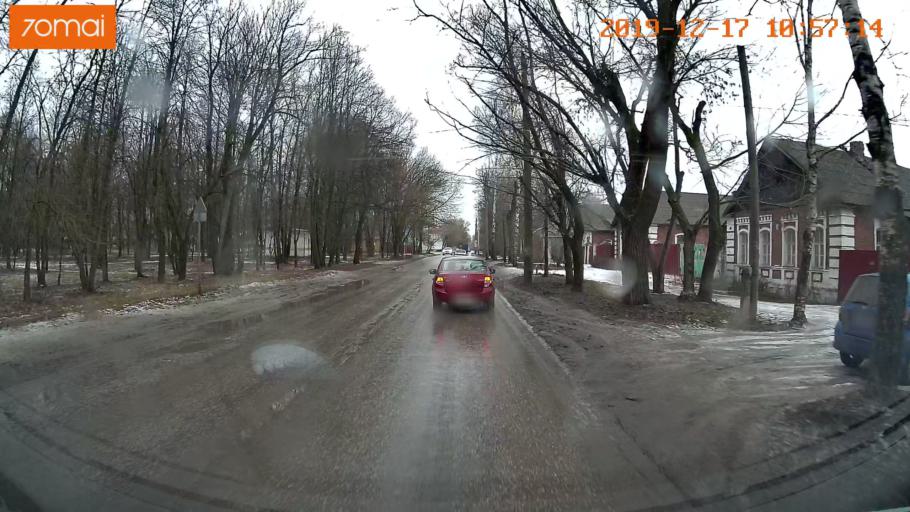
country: RU
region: Vladimir
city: Gus'-Khrustal'nyy
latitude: 55.6205
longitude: 40.6597
